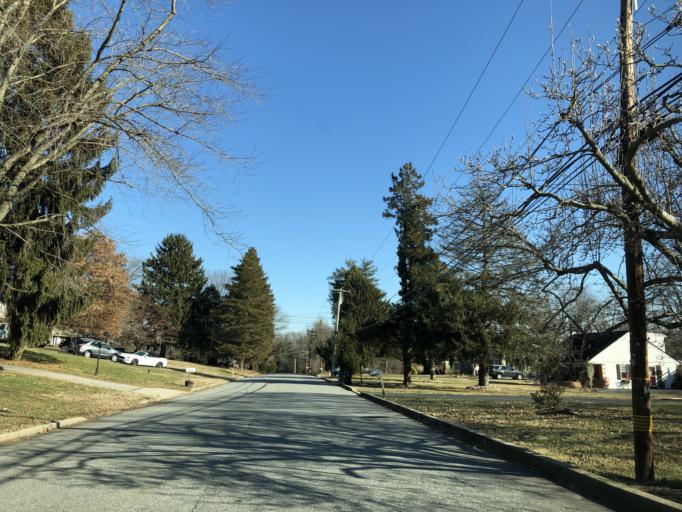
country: US
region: Pennsylvania
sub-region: Delaware County
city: Boothwyn
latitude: 39.8457
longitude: -75.4418
